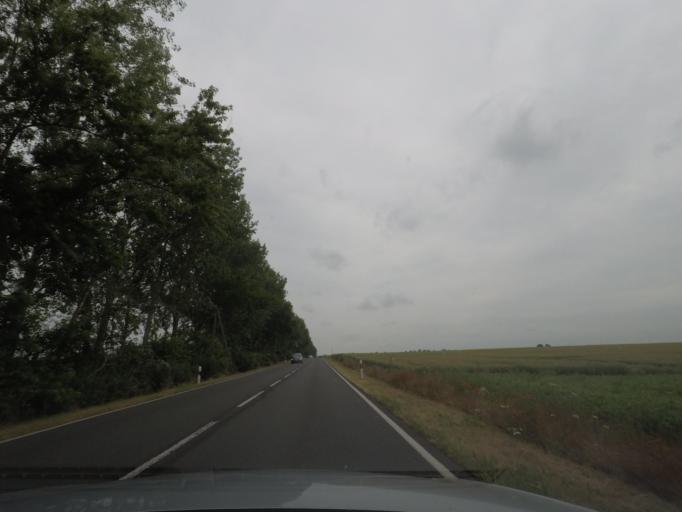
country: DE
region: Saxony-Anhalt
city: Wanzleben
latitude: 52.0465
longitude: 11.4178
